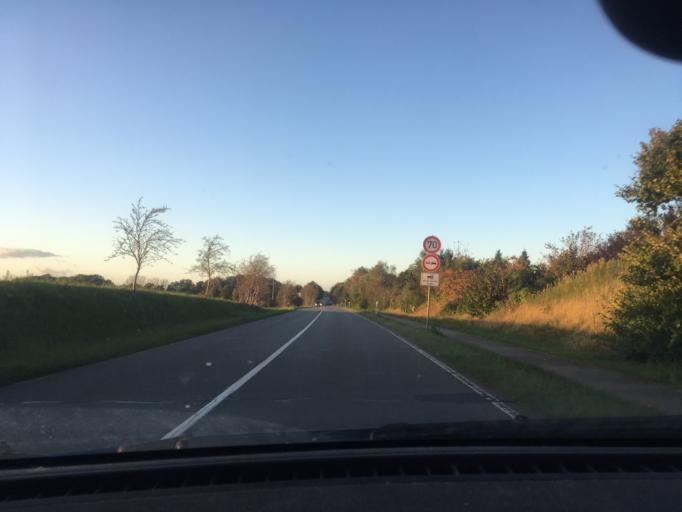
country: DE
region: Lower Saxony
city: Wendisch Evern
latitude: 53.2133
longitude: 10.4658
